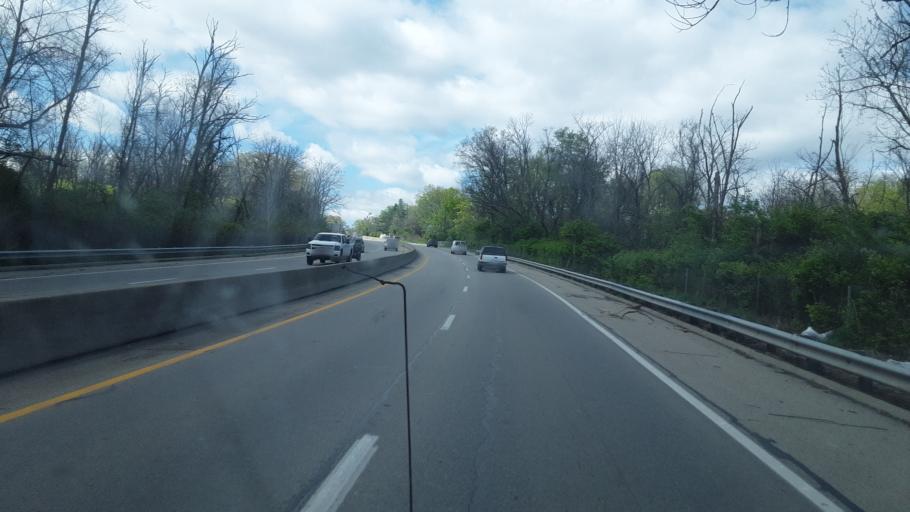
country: US
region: Ohio
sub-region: Hamilton County
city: Dillonvale
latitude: 39.2208
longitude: -84.4163
